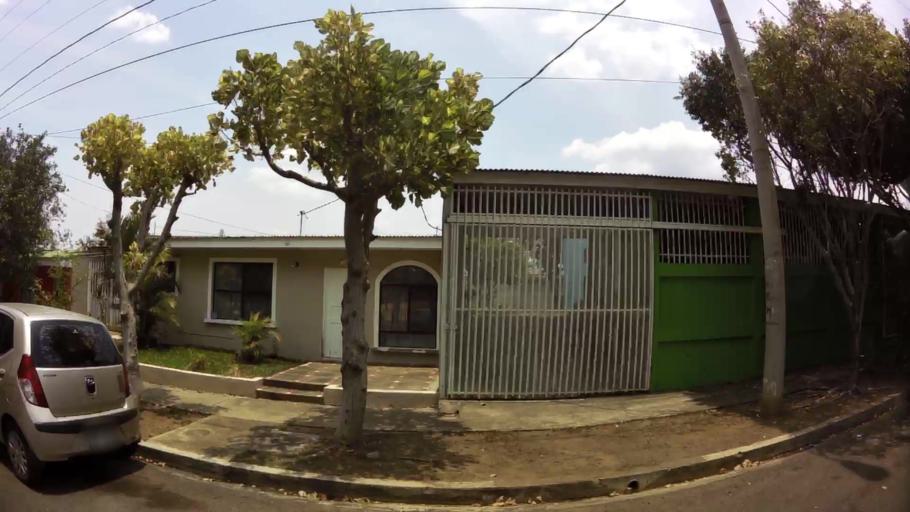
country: NI
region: Managua
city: Managua
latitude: 12.1202
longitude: -86.2859
